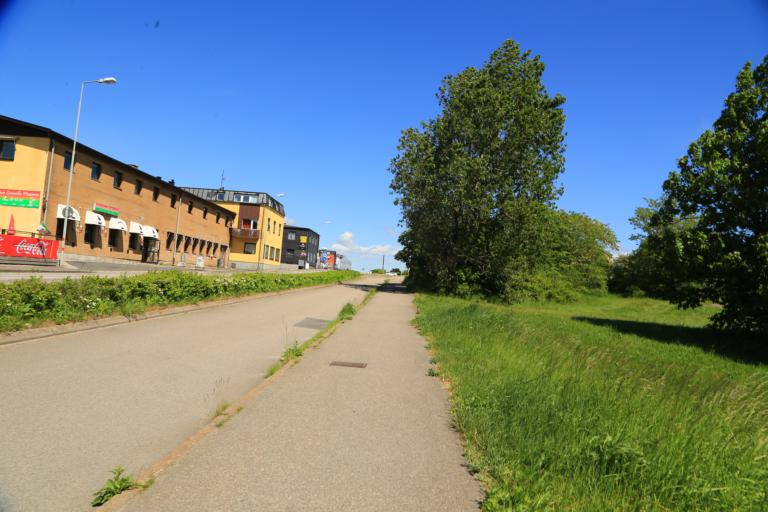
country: SE
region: Halland
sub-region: Varbergs Kommun
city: Varberg
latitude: 57.1131
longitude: 12.2510
